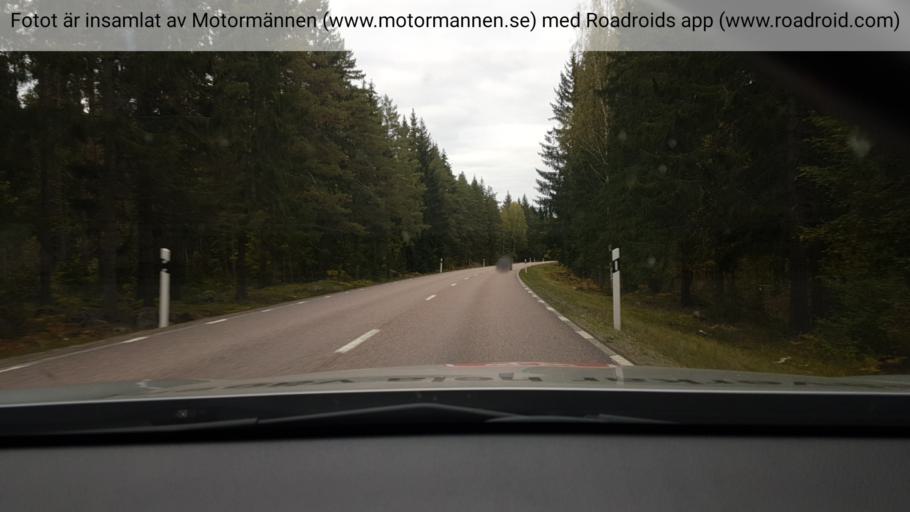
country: SE
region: Gaevleborg
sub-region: Gavle Kommun
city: Hedesunda
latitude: 60.3276
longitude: 16.9194
